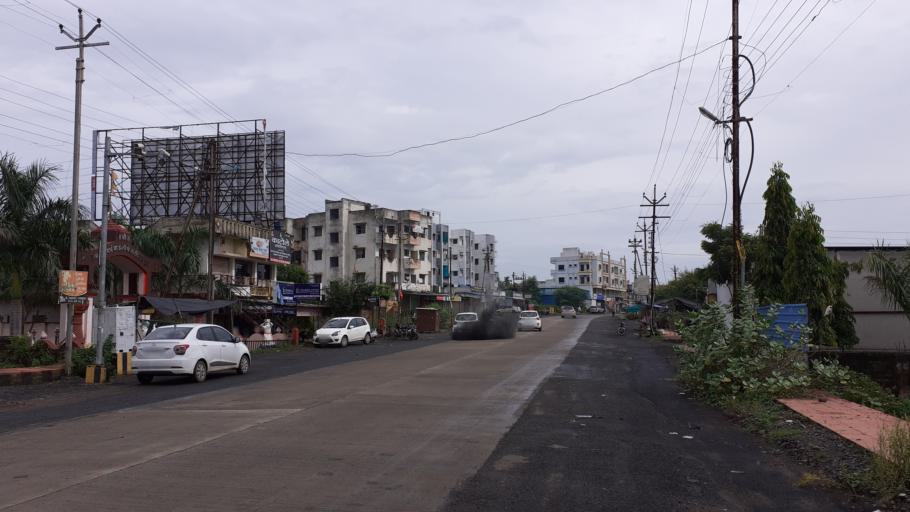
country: IN
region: Maharashtra
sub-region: Nagpur Division
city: Nagpur
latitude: 21.0827
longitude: 79.0959
